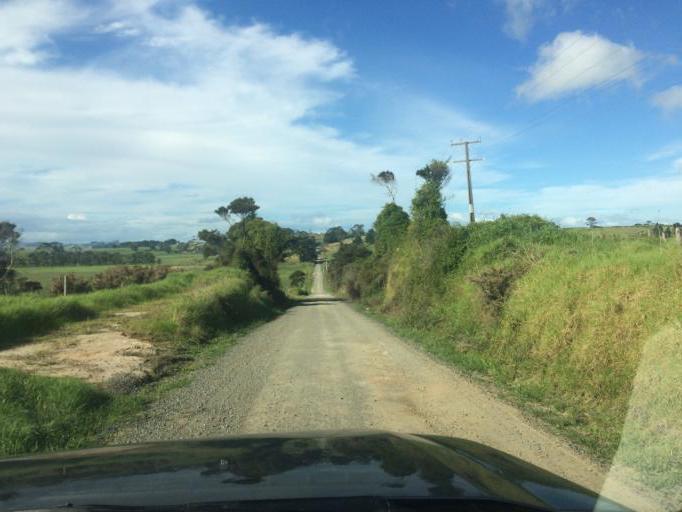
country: NZ
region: Northland
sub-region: Kaipara District
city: Dargaville
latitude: -36.0281
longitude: 173.8679
